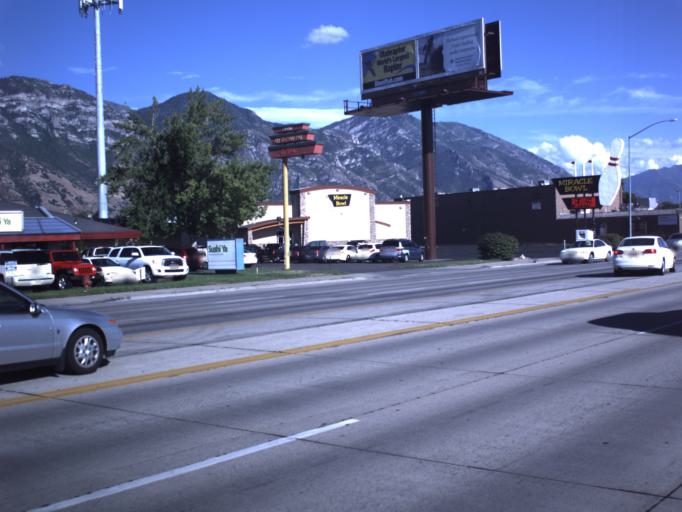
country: US
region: Utah
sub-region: Utah County
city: Orem
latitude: 40.2692
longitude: -111.6829
